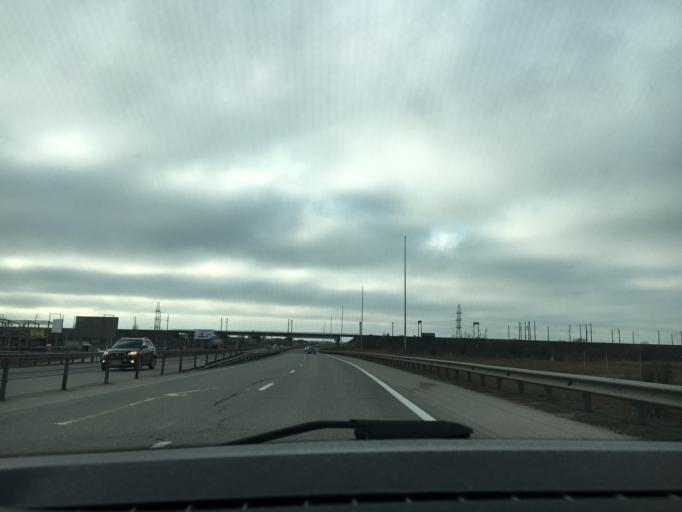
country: RU
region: Rostov
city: Bataysk
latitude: 47.1466
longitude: 39.7027
